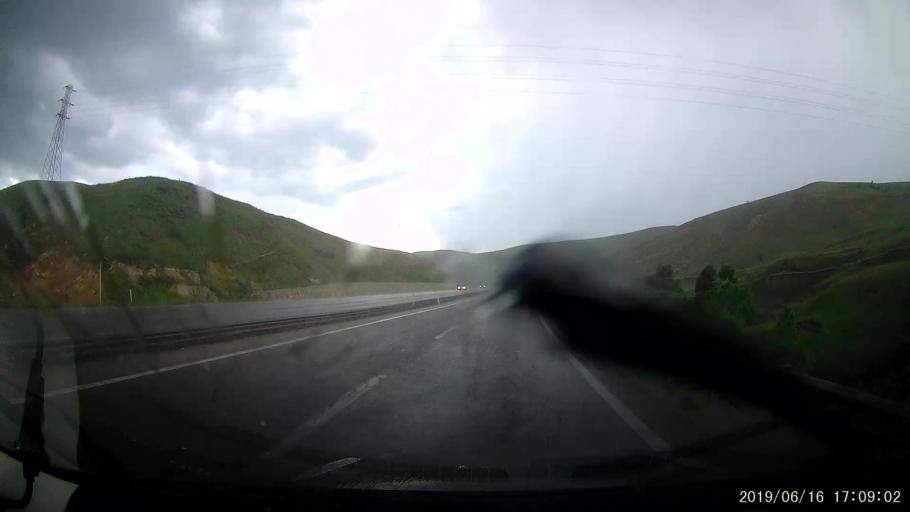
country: TR
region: Erzurum
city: Askale
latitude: 39.9002
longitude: 40.6548
